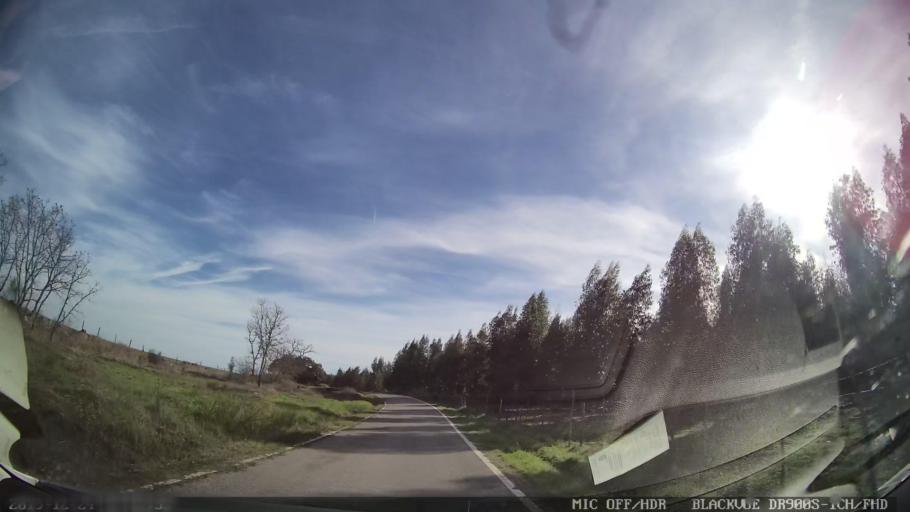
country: PT
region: Portalegre
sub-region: Nisa
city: Nisa
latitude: 39.4942
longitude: -7.7526
